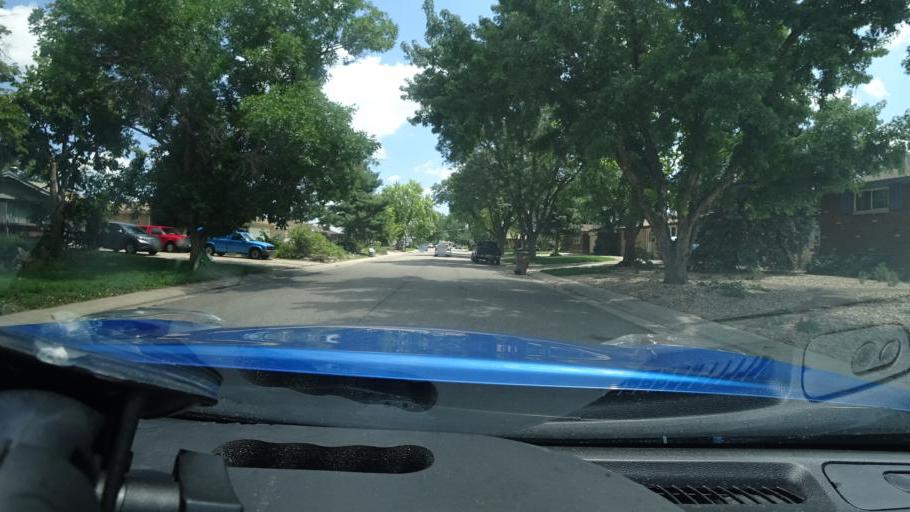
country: US
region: Colorado
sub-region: Adams County
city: Aurora
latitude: 39.7105
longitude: -104.8462
